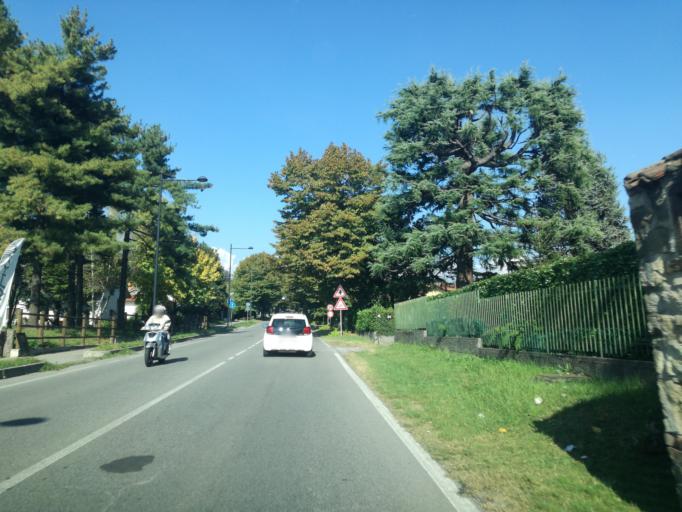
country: IT
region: Lombardy
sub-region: Provincia di Lecco
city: Robbiate
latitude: 45.6920
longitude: 9.4369
